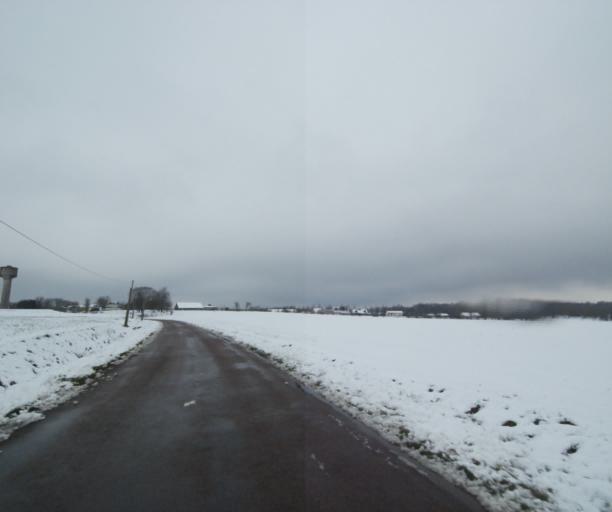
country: FR
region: Champagne-Ardenne
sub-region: Departement de la Haute-Marne
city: Laneuville-a-Remy
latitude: 48.5068
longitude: 4.8511
